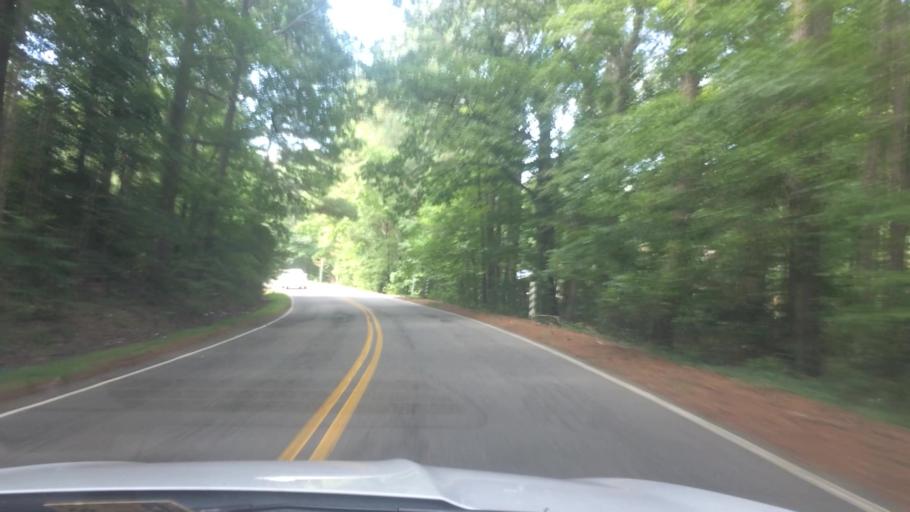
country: US
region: Virginia
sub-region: York County
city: Yorktown
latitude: 37.1731
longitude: -76.4382
